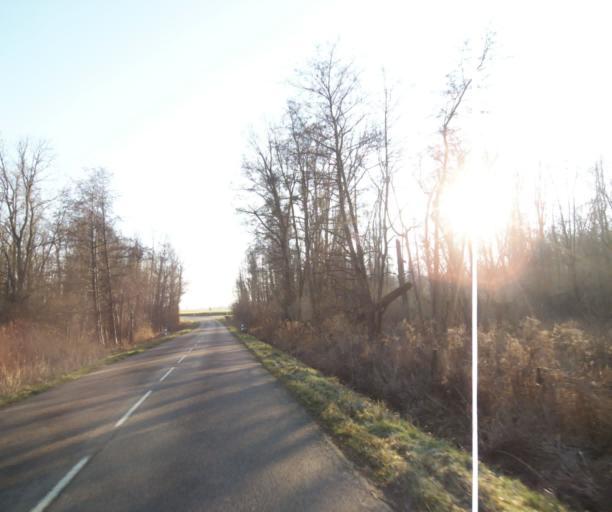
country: FR
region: Champagne-Ardenne
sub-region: Departement de la Haute-Marne
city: Bienville
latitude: 48.5918
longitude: 5.0807
